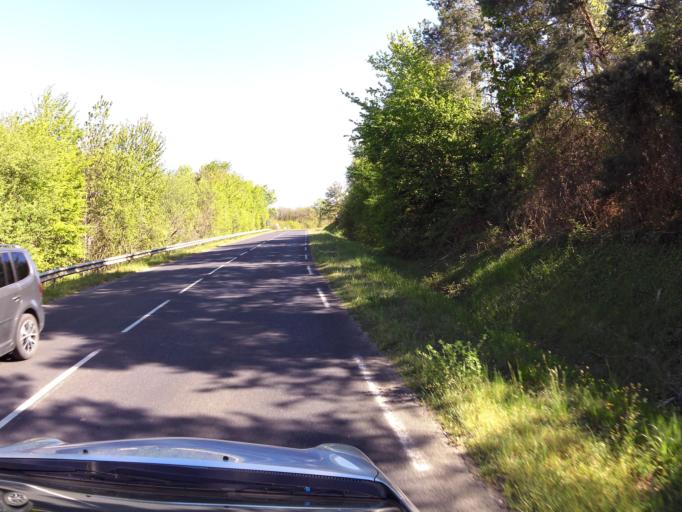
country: FR
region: Aquitaine
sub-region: Departement de la Dordogne
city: Montignac
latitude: 45.0311
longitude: 1.2273
